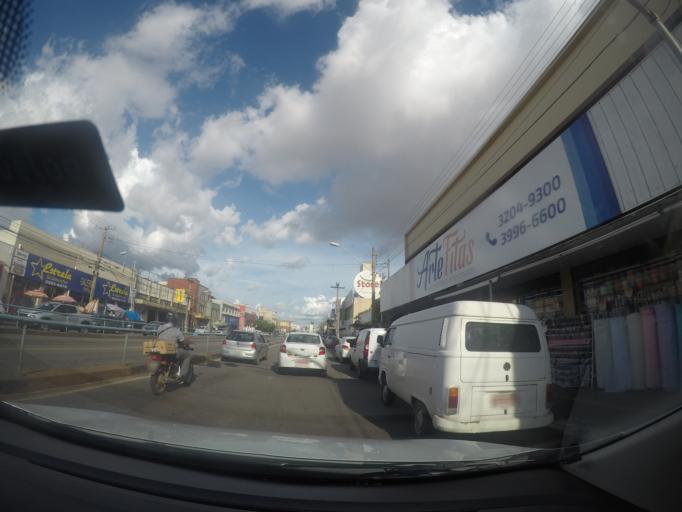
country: BR
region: Goias
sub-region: Goiania
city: Goiania
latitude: -16.6719
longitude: -49.2919
